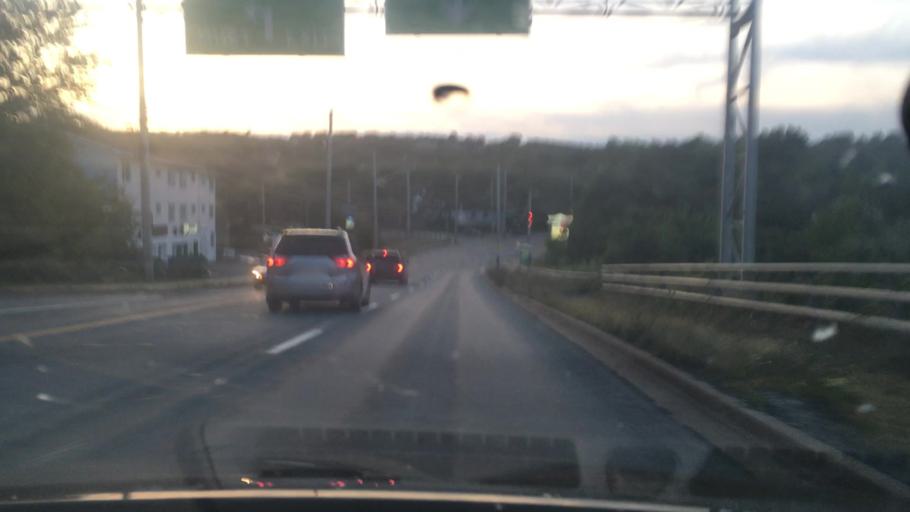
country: CA
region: Nova Scotia
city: Dartmouth
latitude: 44.6812
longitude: -63.6584
